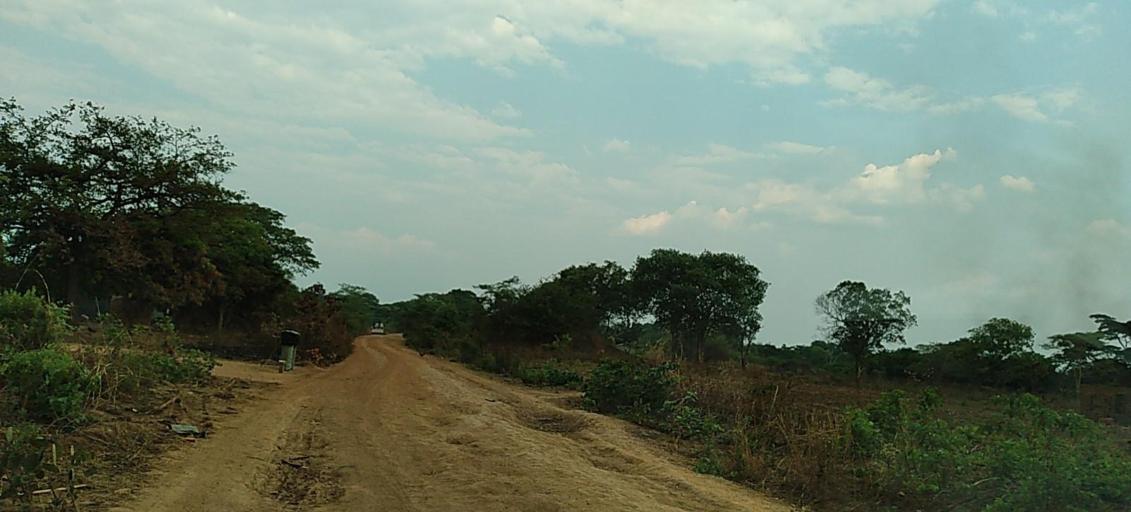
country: ZM
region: Copperbelt
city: Kalulushi
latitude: -13.0185
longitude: 27.9159
